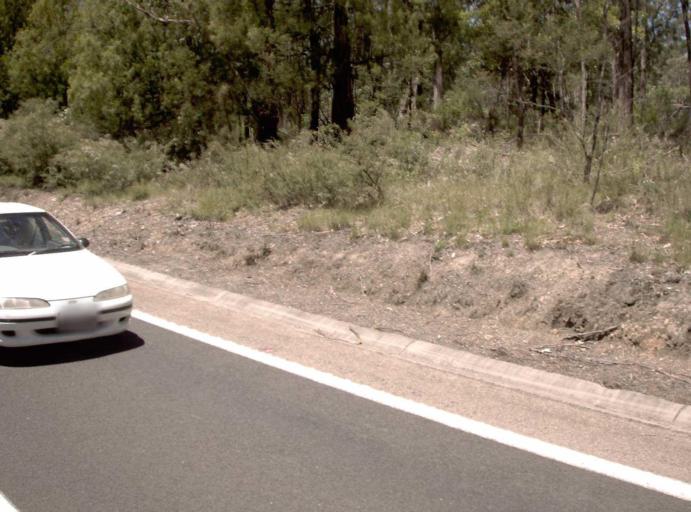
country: AU
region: Victoria
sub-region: East Gippsland
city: Lakes Entrance
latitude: -37.7062
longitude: 148.5756
